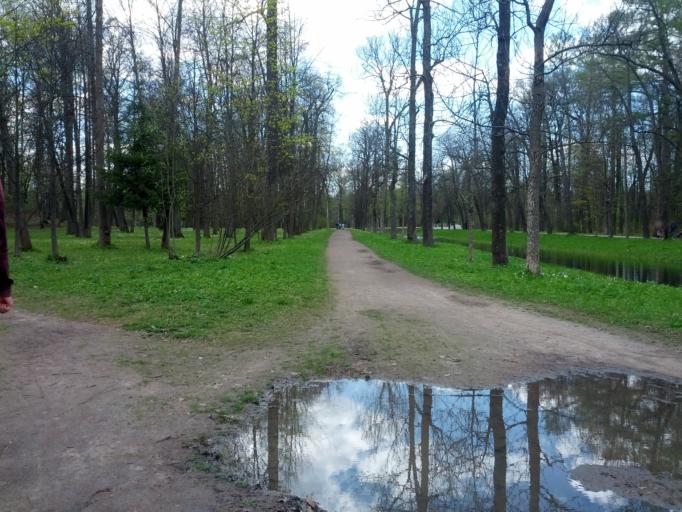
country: RU
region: St.-Petersburg
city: Pushkin
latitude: 59.7197
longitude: 30.3906
